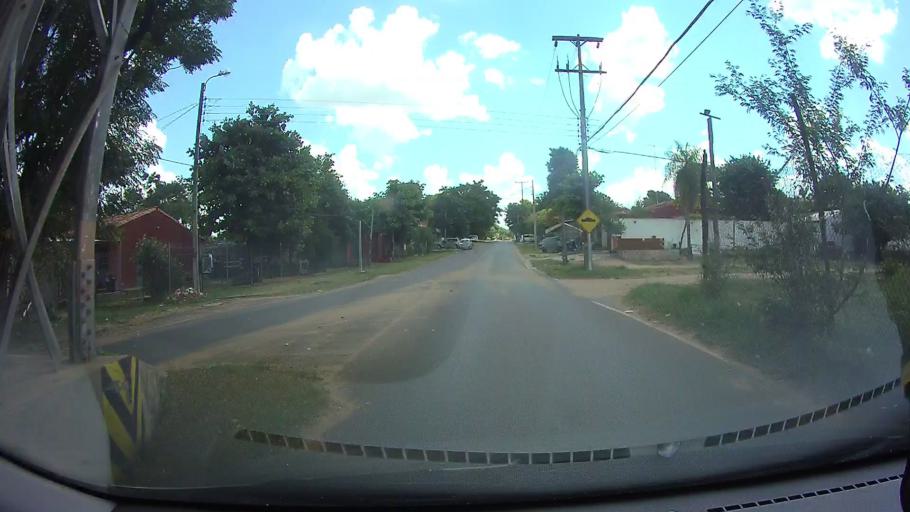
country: PY
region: Central
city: Limpio
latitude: -25.1673
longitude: -57.4361
